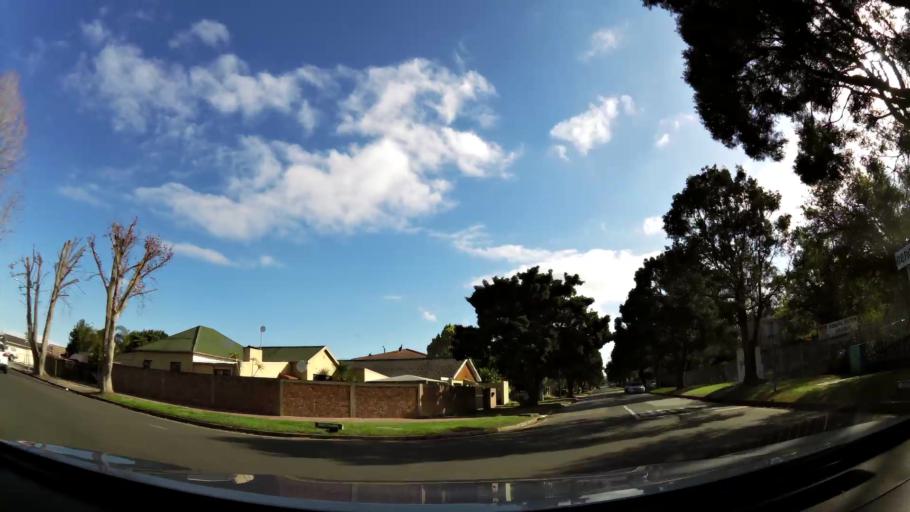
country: ZA
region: Western Cape
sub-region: Eden District Municipality
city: George
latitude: -33.9569
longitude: 22.4751
